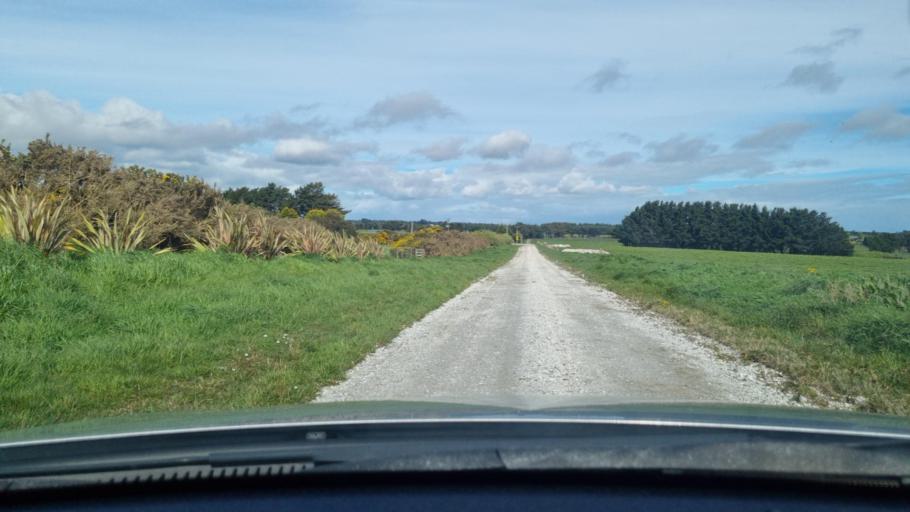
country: NZ
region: Southland
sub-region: Invercargill City
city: Invercargill
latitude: -46.4564
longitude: 168.3862
